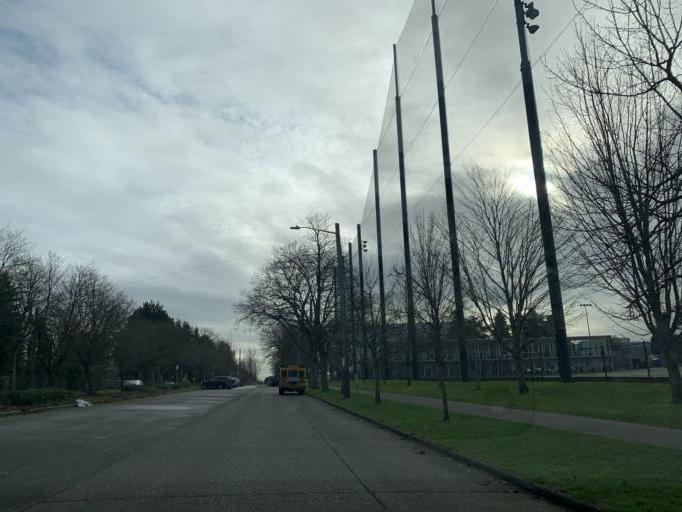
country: US
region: Washington
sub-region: King County
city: Seattle
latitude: 47.5685
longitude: -122.3073
